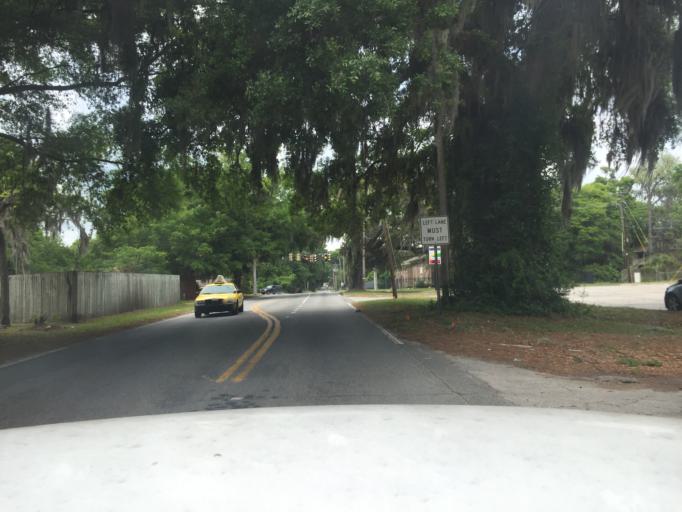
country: US
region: Georgia
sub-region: Chatham County
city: Thunderbolt
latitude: 32.0162
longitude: -81.0664
